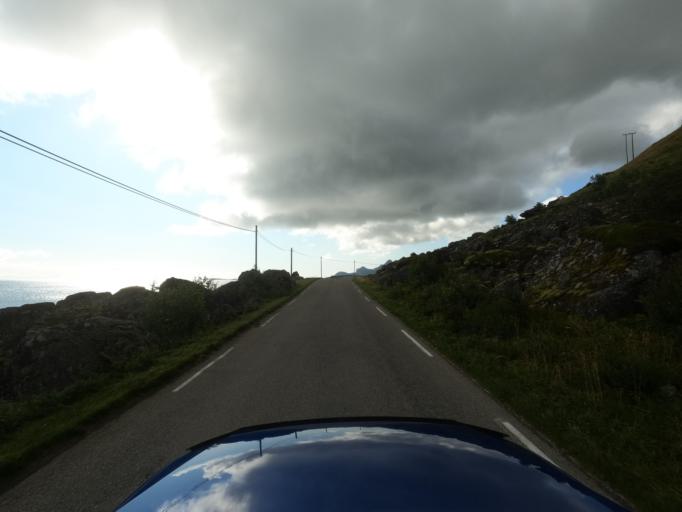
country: NO
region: Nordland
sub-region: Vestvagoy
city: Evjen
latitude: 68.1847
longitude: 13.9277
